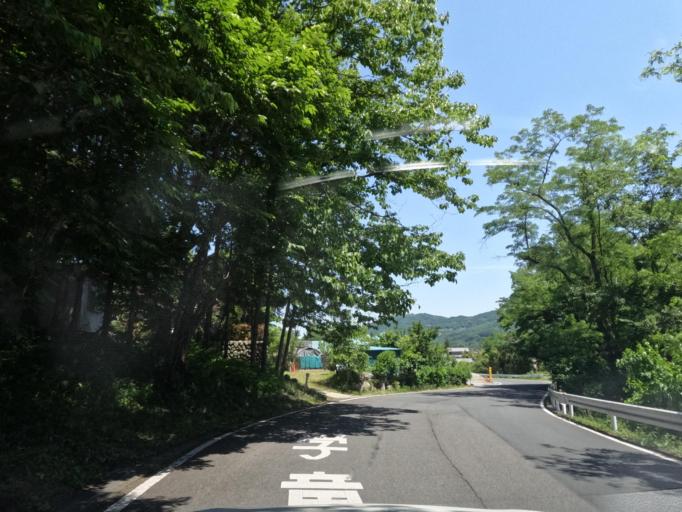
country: JP
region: Saitama
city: Chichibu
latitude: 36.0176
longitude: 139.1063
